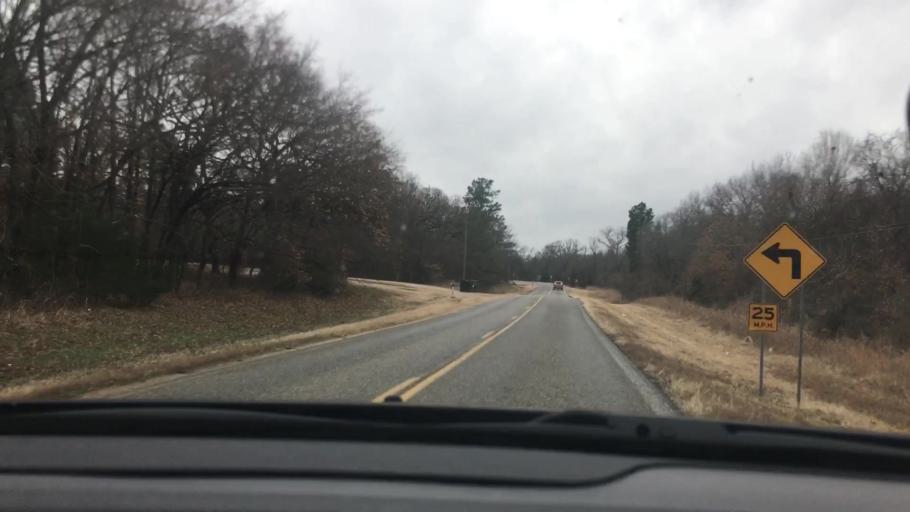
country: US
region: Oklahoma
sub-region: Johnston County
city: Tishomingo
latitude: 34.2123
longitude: -96.6362
